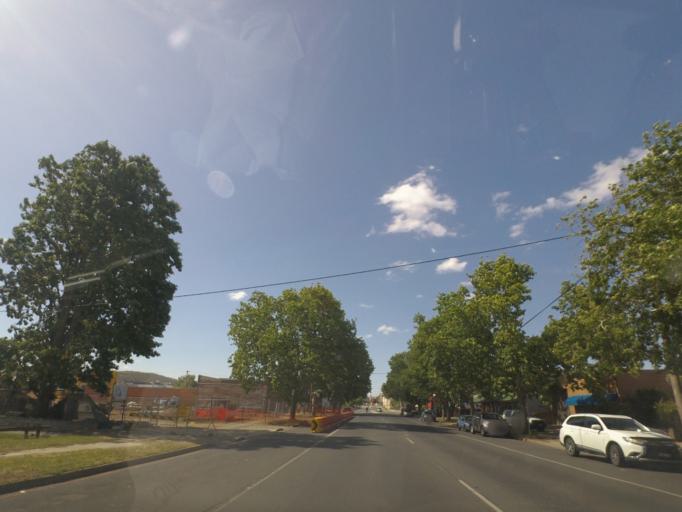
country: AU
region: New South Wales
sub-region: Albury Municipality
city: South Albury
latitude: -36.0860
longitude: 146.9146
